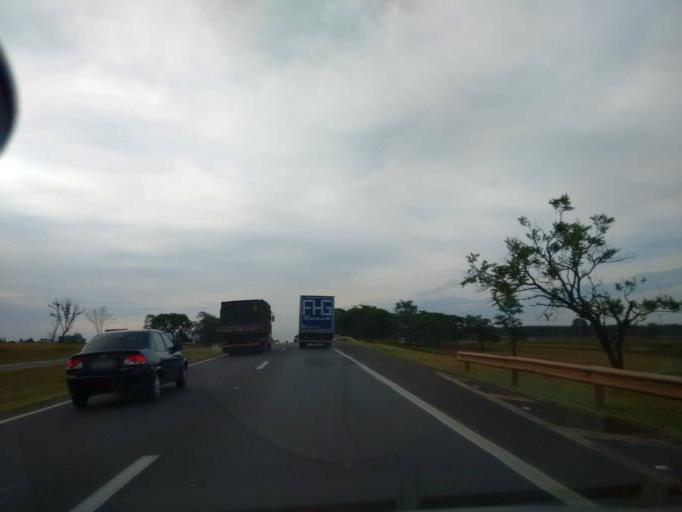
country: BR
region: Sao Paulo
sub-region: Araraquara
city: Araraquara
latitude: -21.7896
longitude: -48.2171
